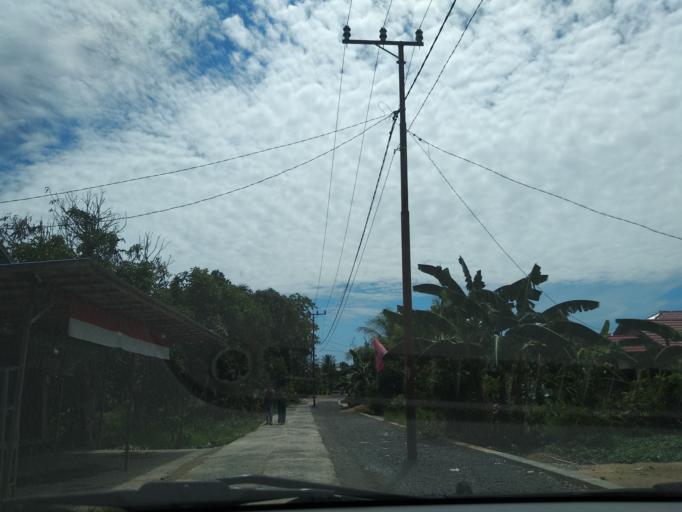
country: ID
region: South Kalimantan
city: Tabunganen
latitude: -3.4103
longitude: 114.4907
